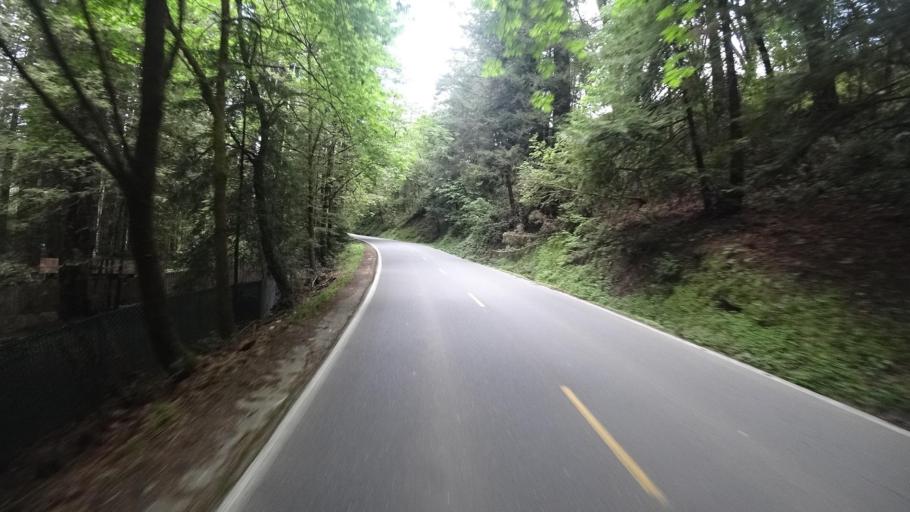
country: US
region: California
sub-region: Humboldt County
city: Redway
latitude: 40.1224
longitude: -123.8330
